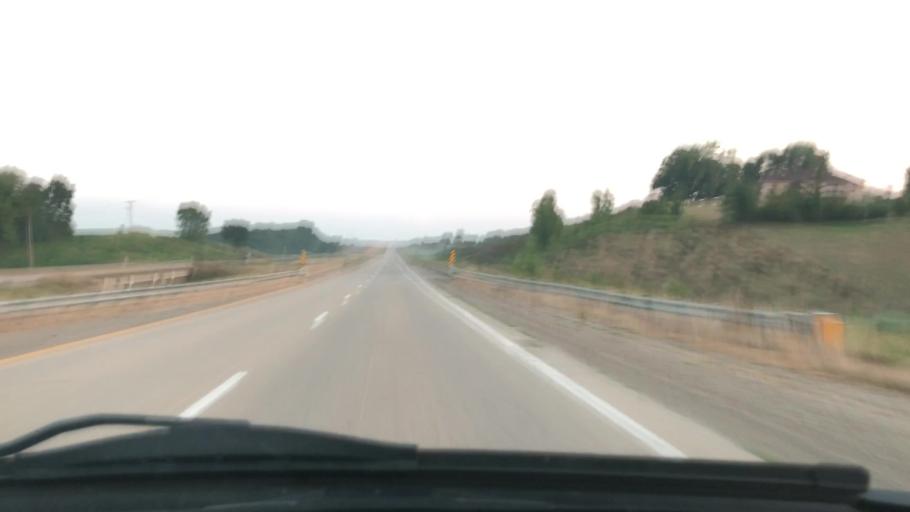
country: US
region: Iowa
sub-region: Henry County
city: Mount Pleasant
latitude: 40.8626
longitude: -91.5651
